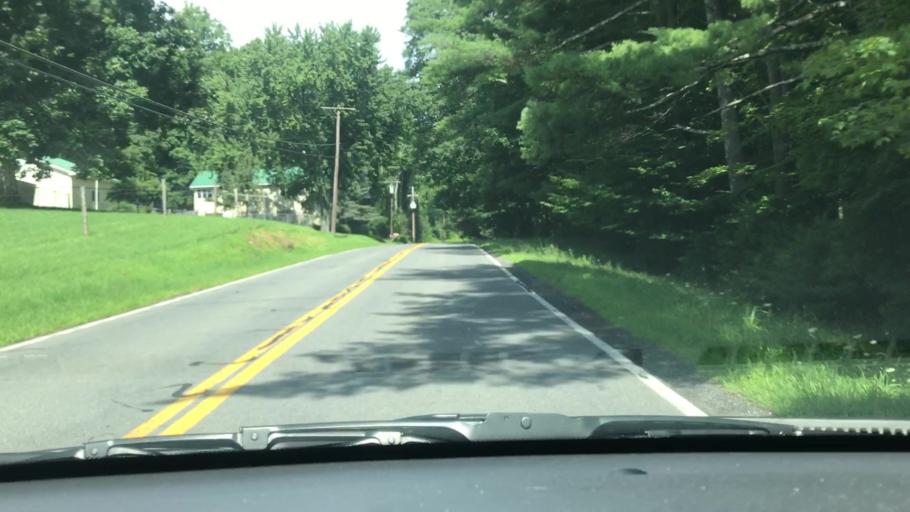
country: US
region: New York
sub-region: Ulster County
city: Shokan
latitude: 41.9566
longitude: -74.2646
